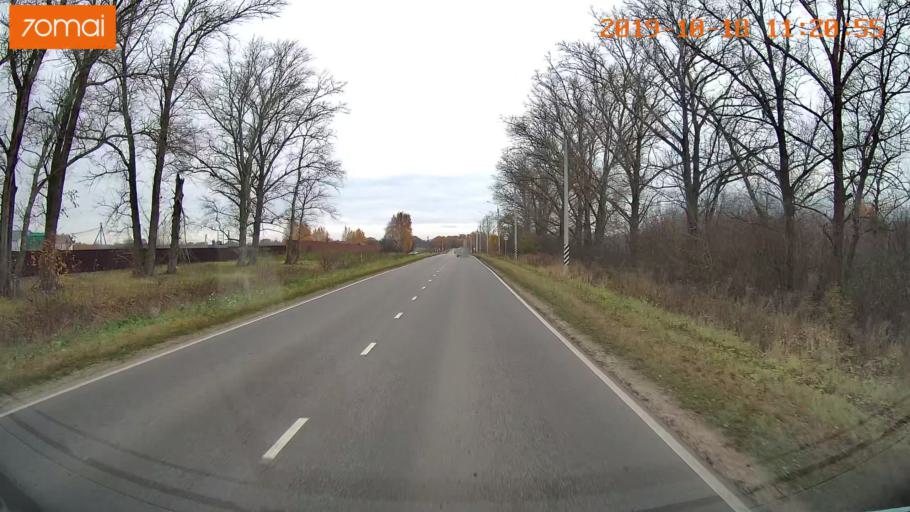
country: RU
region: Tula
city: Kimovsk
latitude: 54.0677
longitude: 38.5614
